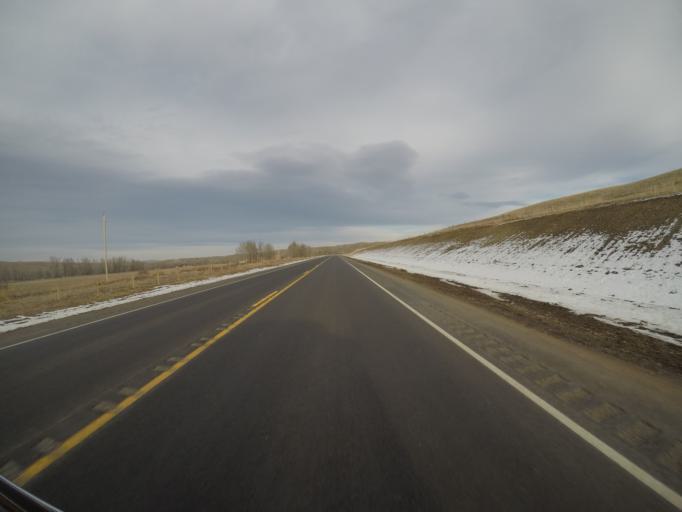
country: US
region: Montana
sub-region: Stillwater County
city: Absarokee
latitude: 45.4381
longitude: -109.4575
